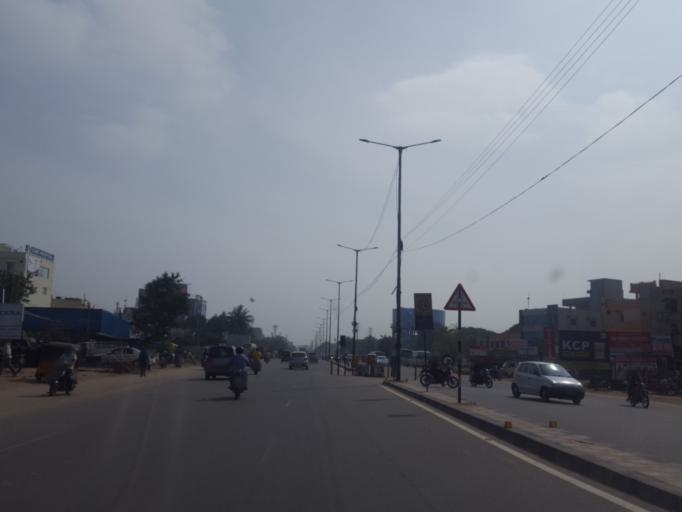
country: IN
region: Telangana
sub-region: Medak
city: Serilingampalle
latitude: 17.5084
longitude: 78.3016
